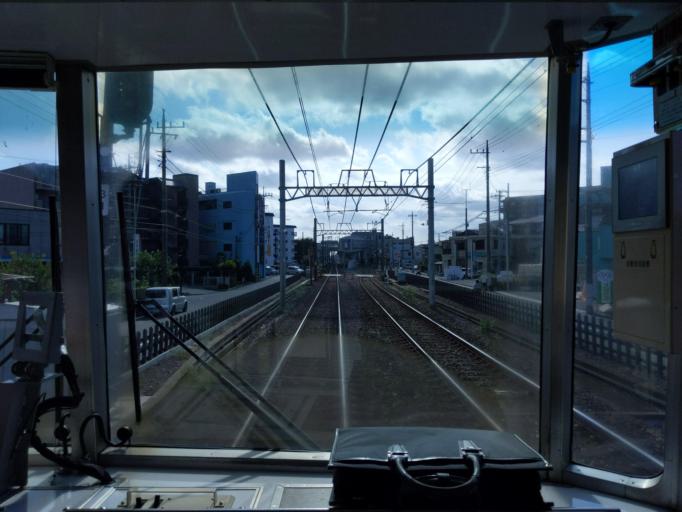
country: JP
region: Chiba
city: Funabashi
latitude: 35.7122
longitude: 140.0402
